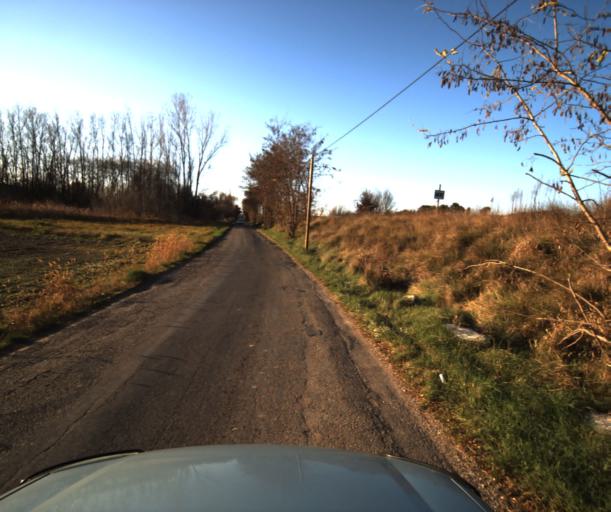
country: FR
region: Provence-Alpes-Cote d'Azur
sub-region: Departement du Vaucluse
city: Pertuis
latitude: 43.6772
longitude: 5.5232
